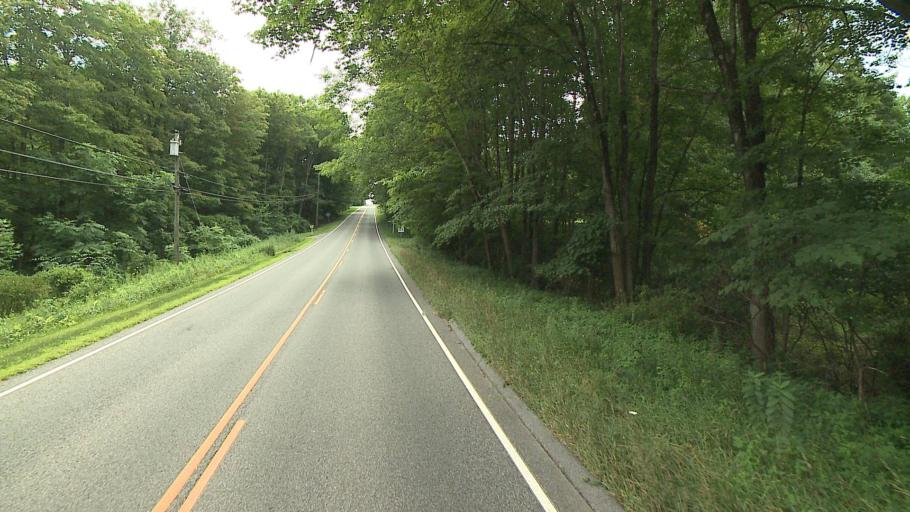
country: US
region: Connecticut
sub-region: Fairfield County
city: Sherman
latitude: 41.6194
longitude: -73.5072
